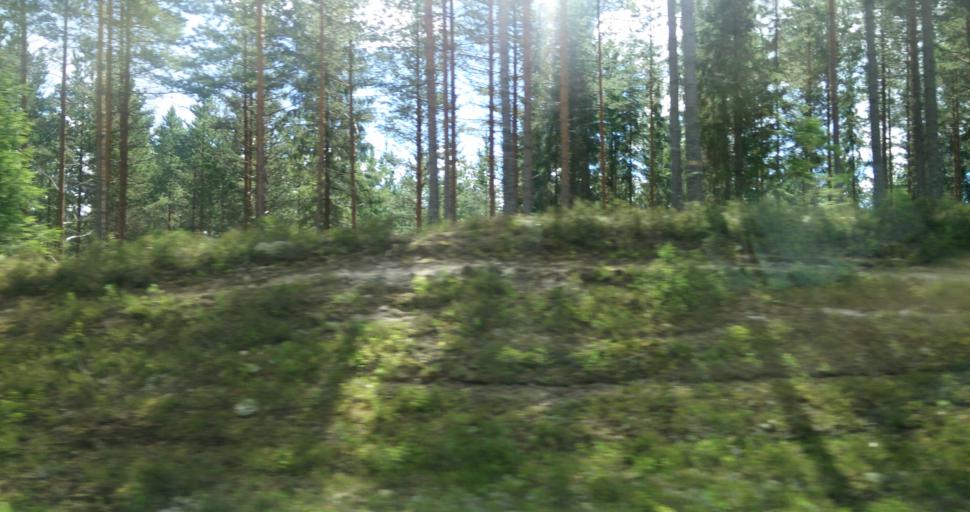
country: SE
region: Vaermland
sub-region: Hagfors Kommun
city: Ekshaerad
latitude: 60.0422
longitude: 13.5183
